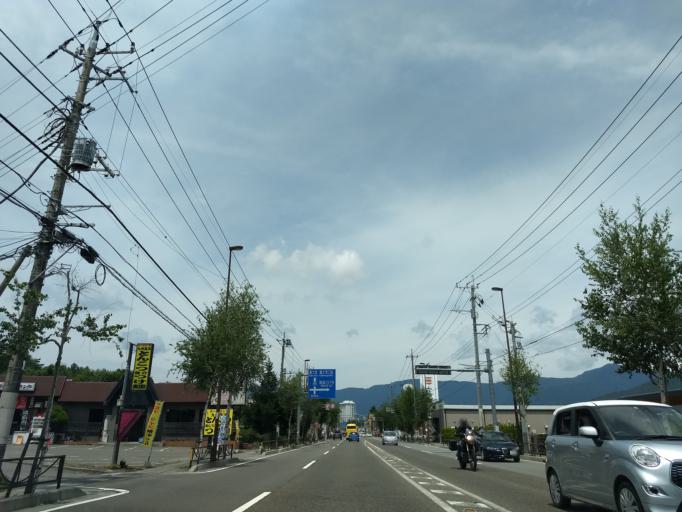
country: JP
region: Yamanashi
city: Fujikawaguchiko
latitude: 35.4783
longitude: 138.7867
